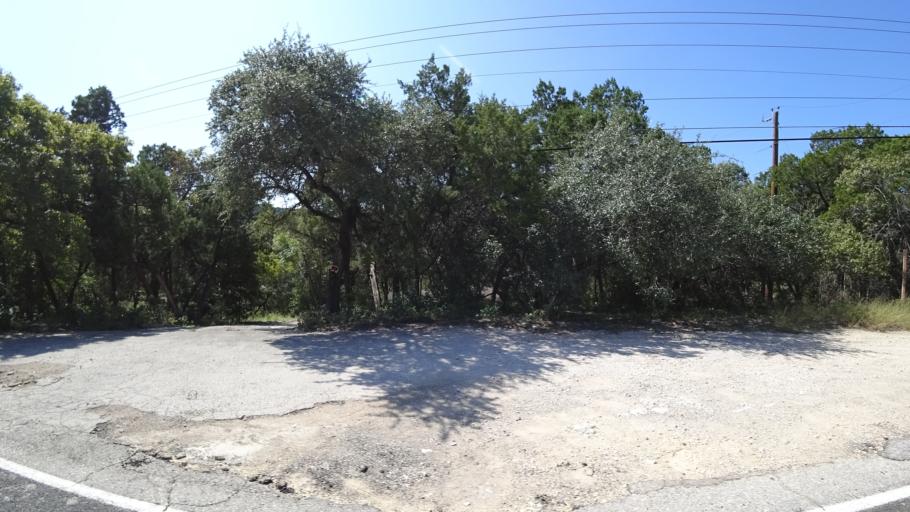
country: US
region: Texas
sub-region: Travis County
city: West Lake Hills
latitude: 30.3066
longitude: -97.7959
